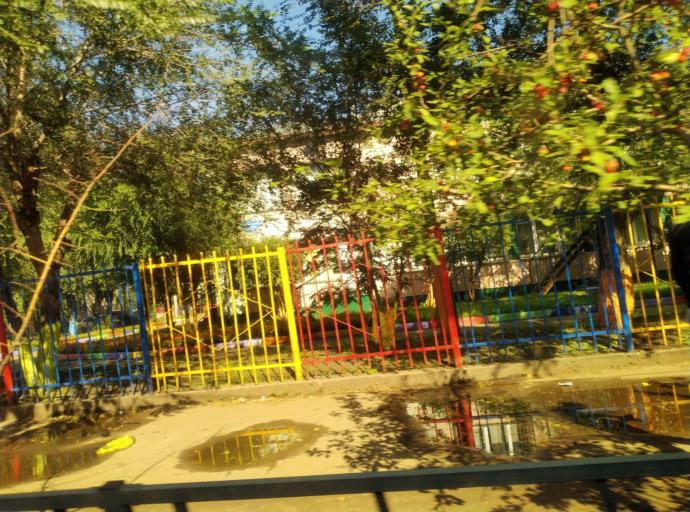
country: RU
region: Krasnoyarskiy
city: Krasnoyarsk
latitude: 55.9782
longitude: 92.8573
